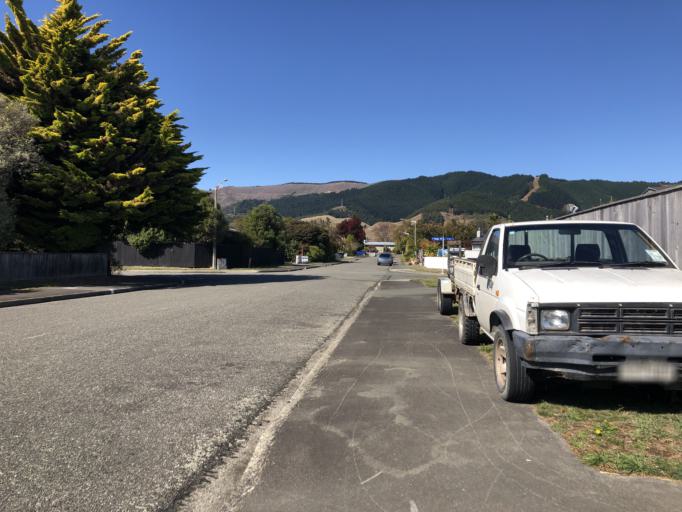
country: NZ
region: Tasman
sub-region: Tasman District
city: Richmond
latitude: -41.3426
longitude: 173.1754
